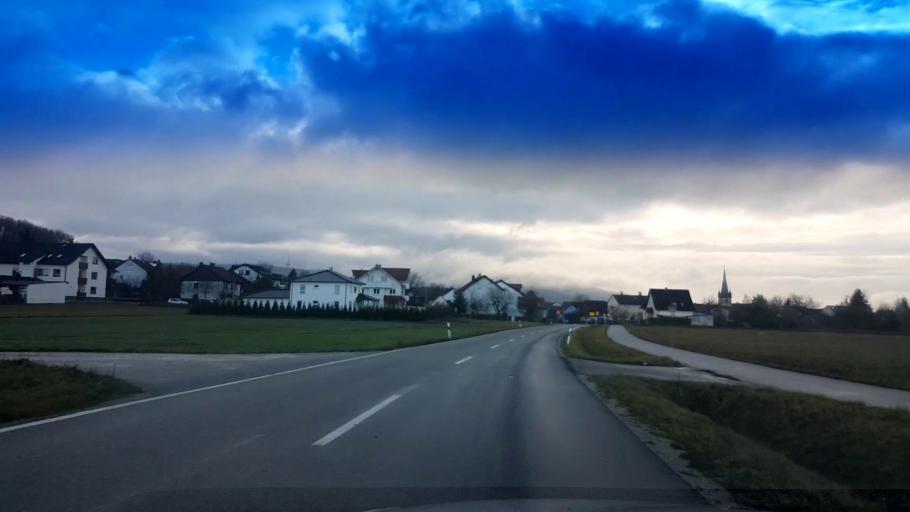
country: DE
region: Bavaria
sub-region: Upper Franconia
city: Litzendorf
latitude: 49.8852
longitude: 11.0123
